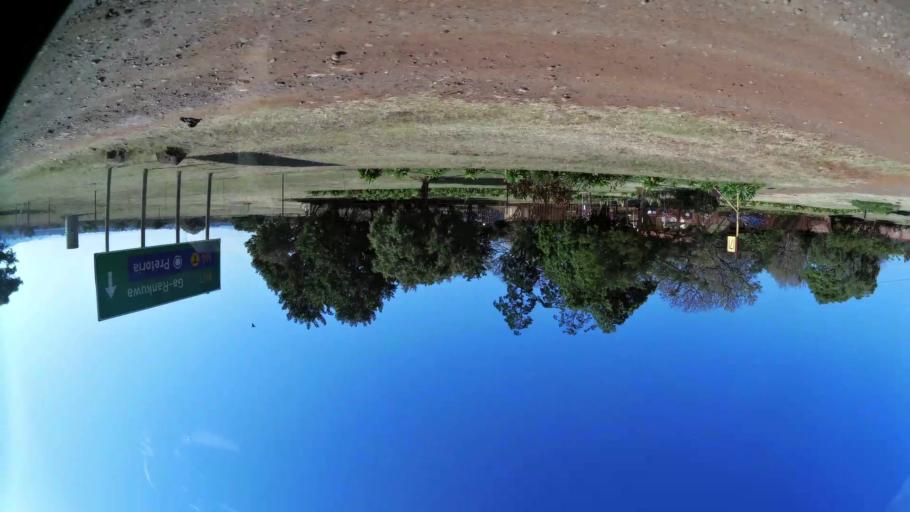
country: ZA
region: North-West
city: Ga-Rankuwa
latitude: -25.6583
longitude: 28.0454
